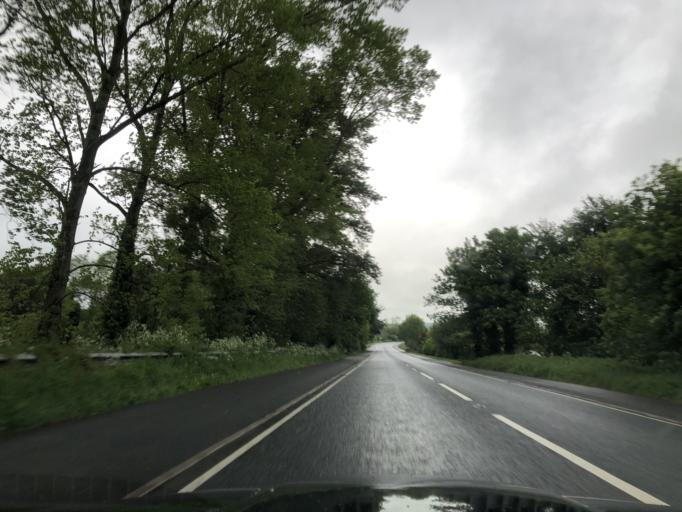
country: GB
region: Northern Ireland
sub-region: Antrim Borough
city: Antrim
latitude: 54.6935
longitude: -6.2266
